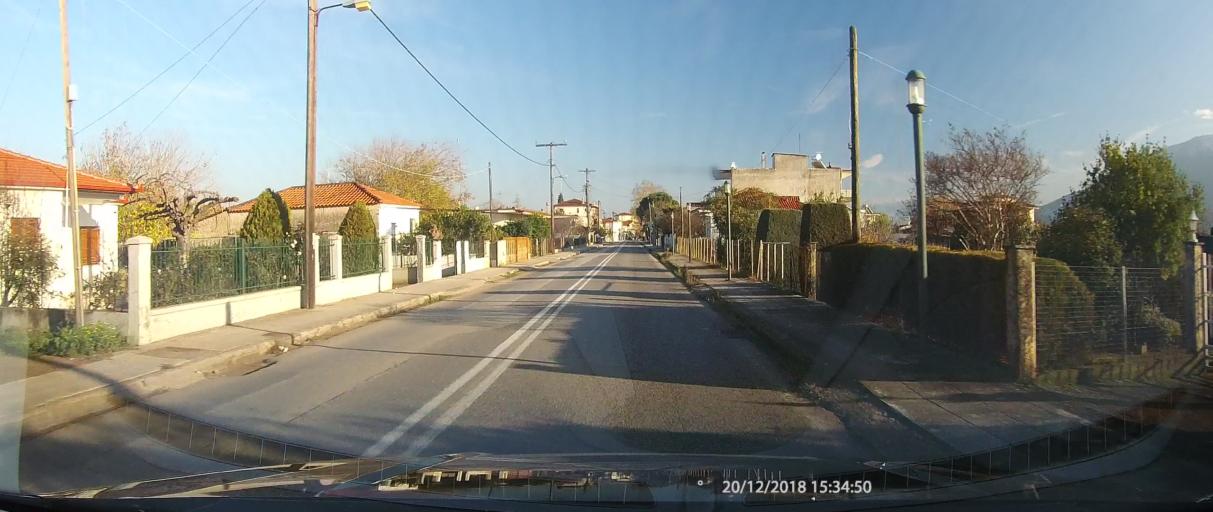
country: GR
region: Central Greece
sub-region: Nomos Fthiotidos
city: Lianokladhion
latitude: 38.9176
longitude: 22.2989
